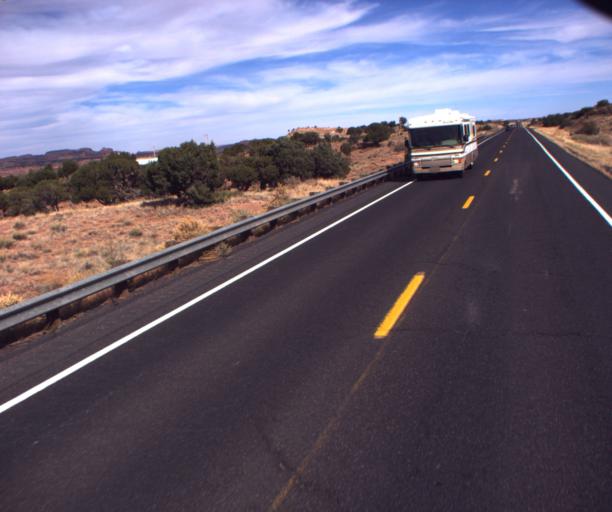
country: US
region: Arizona
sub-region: Navajo County
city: Kayenta
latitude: 36.6949
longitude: -110.3555
